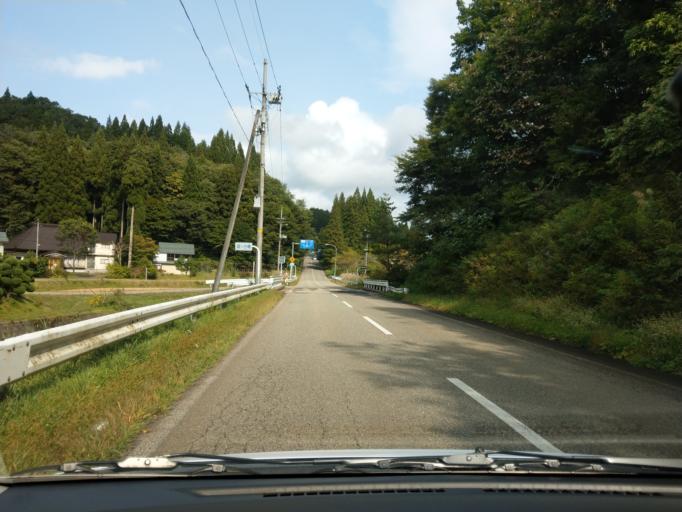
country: JP
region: Akita
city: Omagari
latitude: 39.4651
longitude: 140.3174
